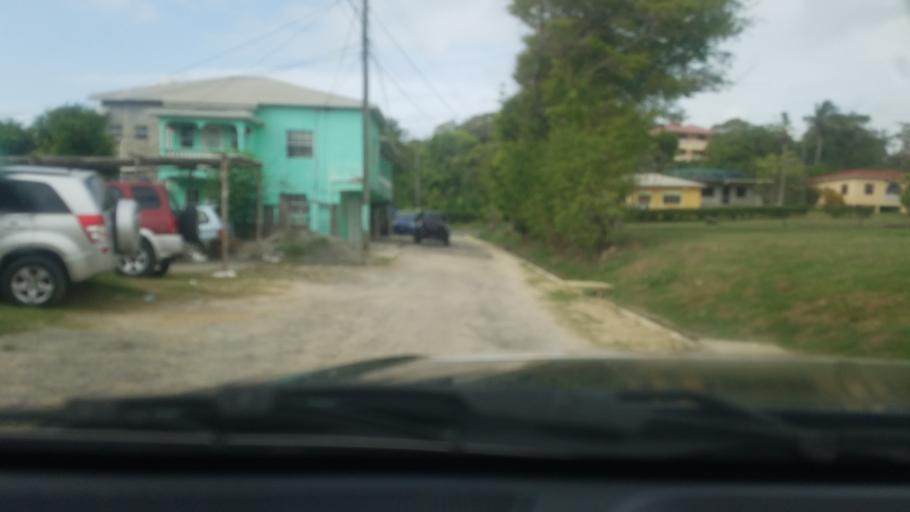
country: LC
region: Micoud Quarter
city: Micoud
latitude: 13.7977
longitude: -60.9149
